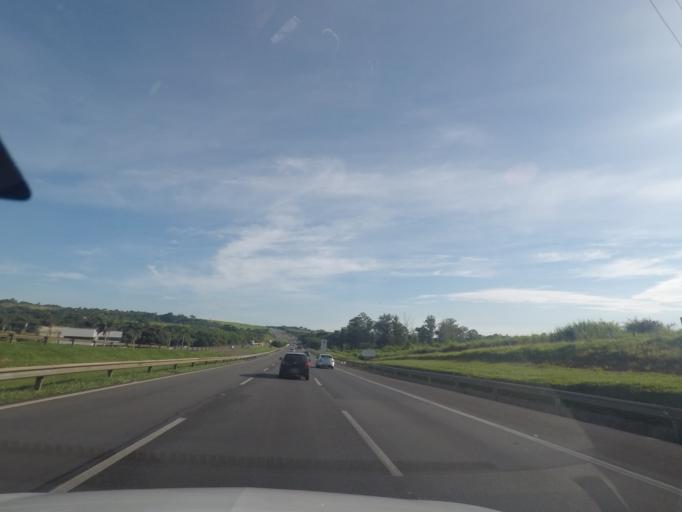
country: BR
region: Sao Paulo
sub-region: Americana
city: Americana
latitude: -22.6907
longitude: -47.3108
